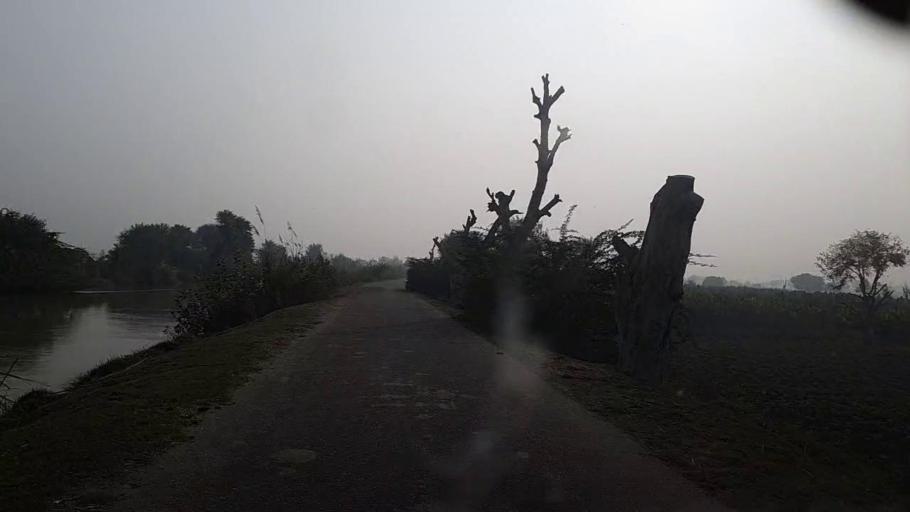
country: PK
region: Sindh
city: Bozdar
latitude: 27.1429
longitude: 68.6569
